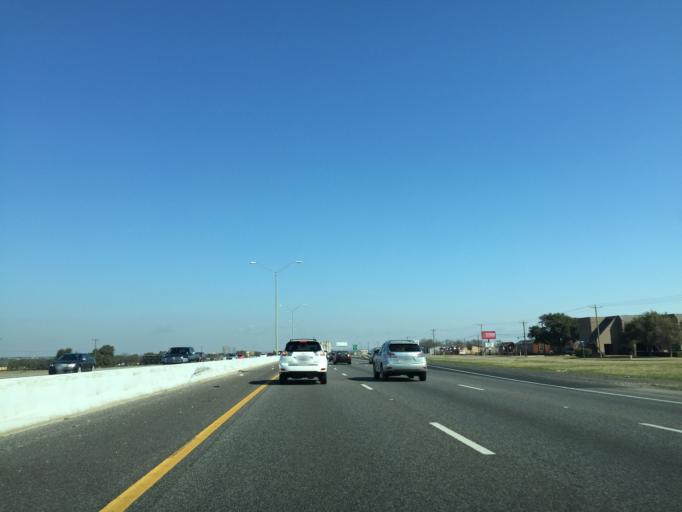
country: US
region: Texas
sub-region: Williamson County
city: Georgetown
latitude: 30.5957
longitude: -97.6900
